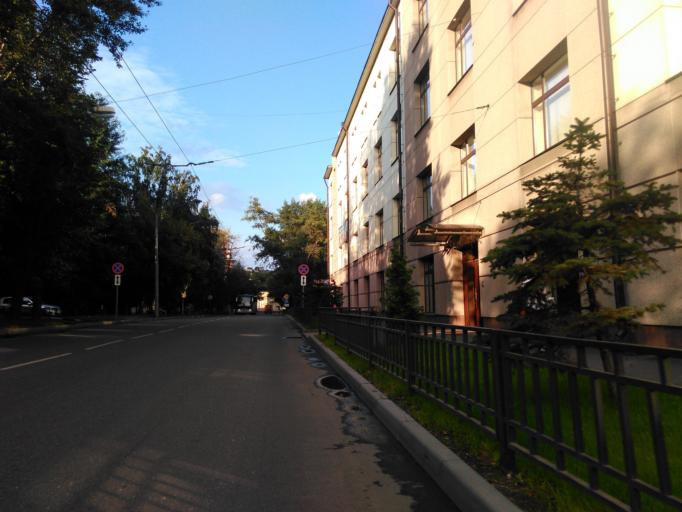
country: RU
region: Moscow
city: Sokol'niki
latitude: 55.7735
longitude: 37.6650
